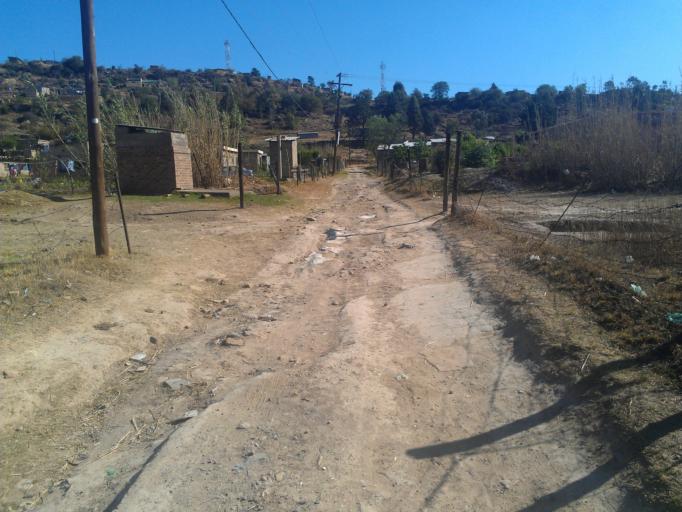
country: LS
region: Maseru
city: Maseru
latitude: -29.3221
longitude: 27.5259
